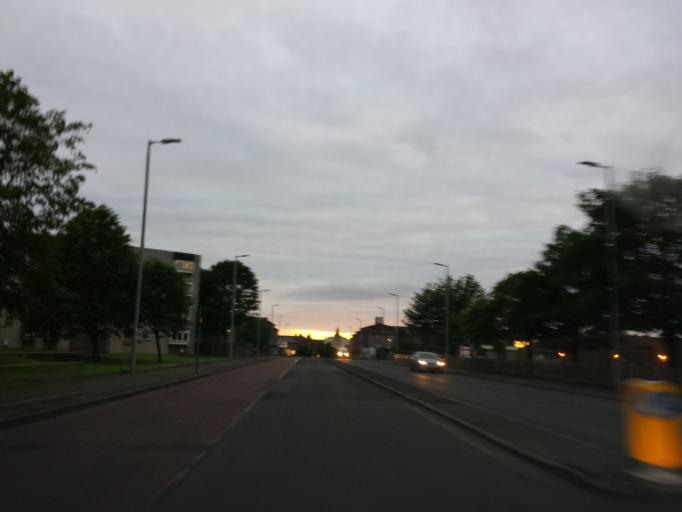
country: GB
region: Scotland
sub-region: South Ayrshire
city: Ayr
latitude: 55.4668
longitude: -4.6230
